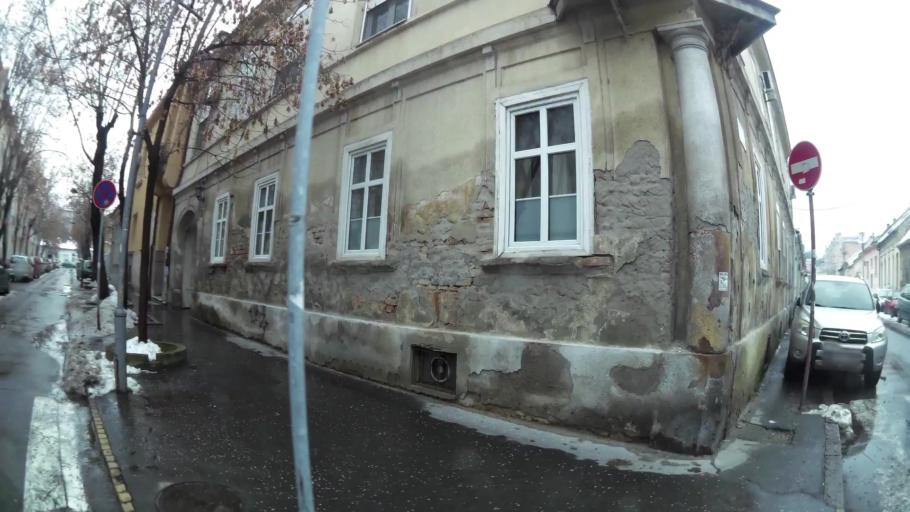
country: RS
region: Central Serbia
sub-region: Belgrade
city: Zemun
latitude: 44.8434
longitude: 20.4099
